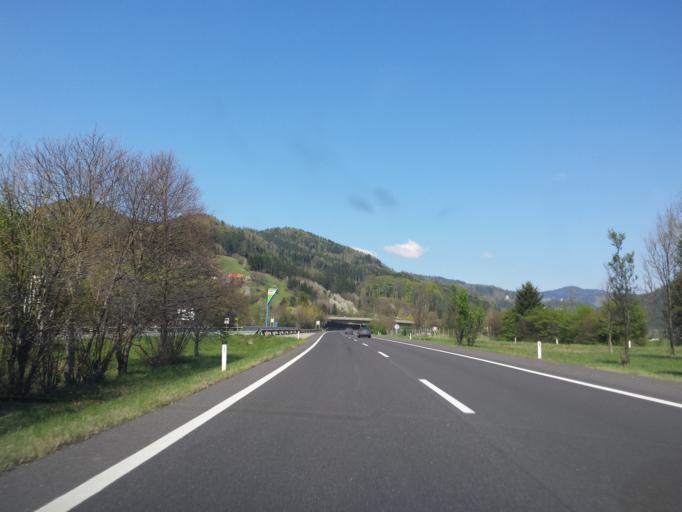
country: AT
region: Styria
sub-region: Politischer Bezirk Graz-Umgebung
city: Deutschfeistritz
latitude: 47.2055
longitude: 15.3180
